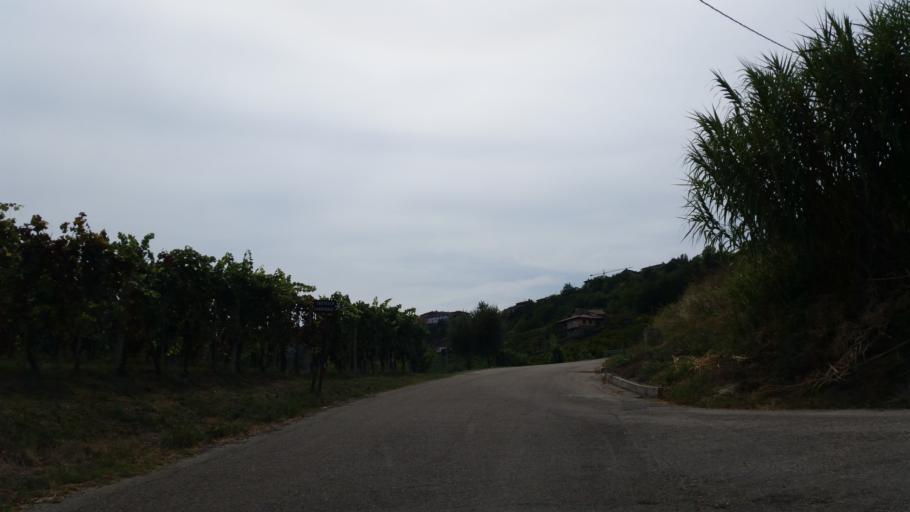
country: IT
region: Piedmont
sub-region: Provincia di Cuneo
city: Diano d'Alba
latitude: 44.6570
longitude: 8.0337
